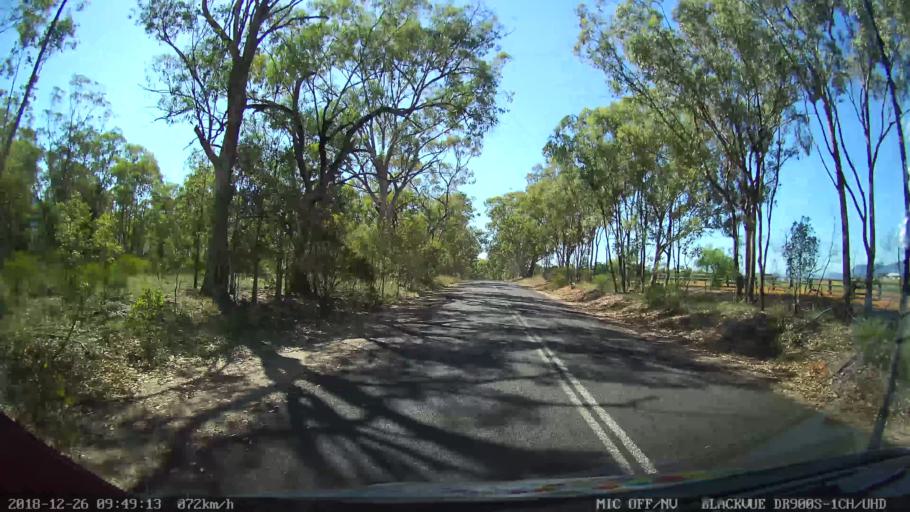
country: AU
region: New South Wales
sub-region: Mid-Western Regional
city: Kandos
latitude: -32.9928
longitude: 150.1214
